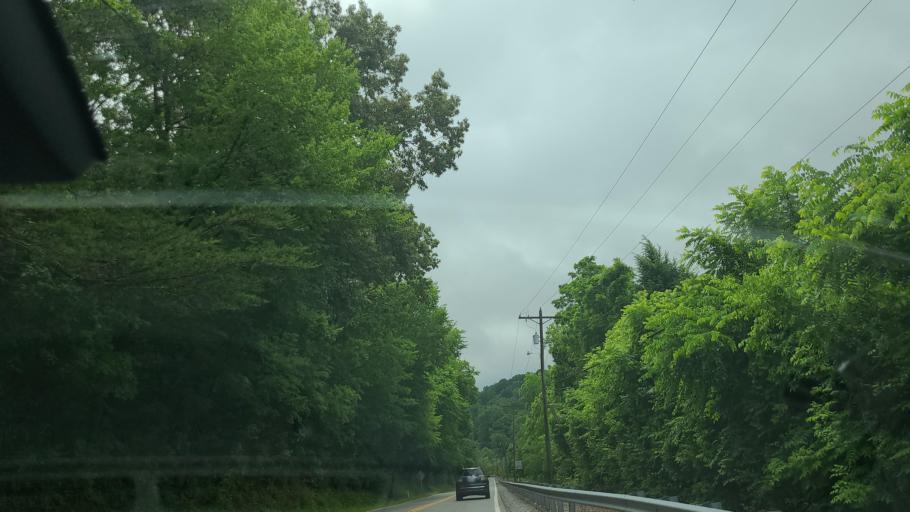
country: US
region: Tennessee
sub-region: Rhea County
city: Dayton
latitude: 35.4949
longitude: -85.0018
